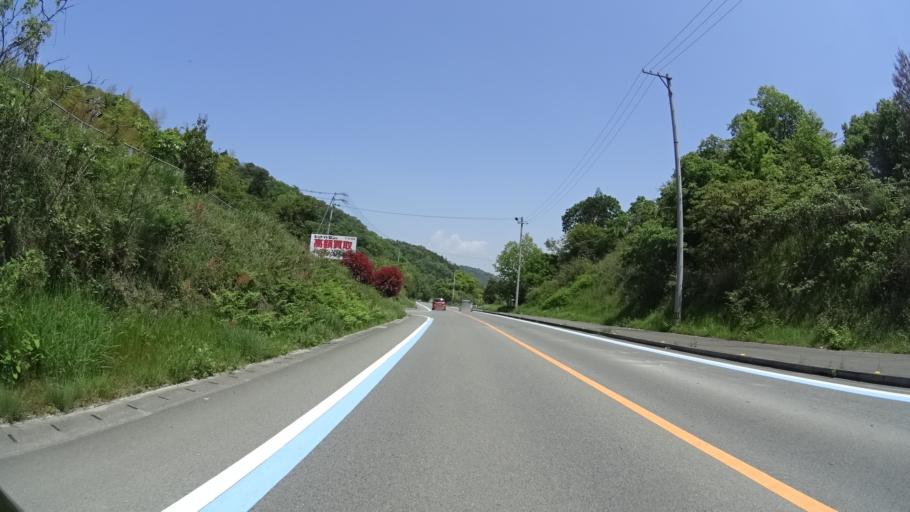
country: JP
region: Ehime
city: Iyo
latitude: 33.7195
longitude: 132.6775
